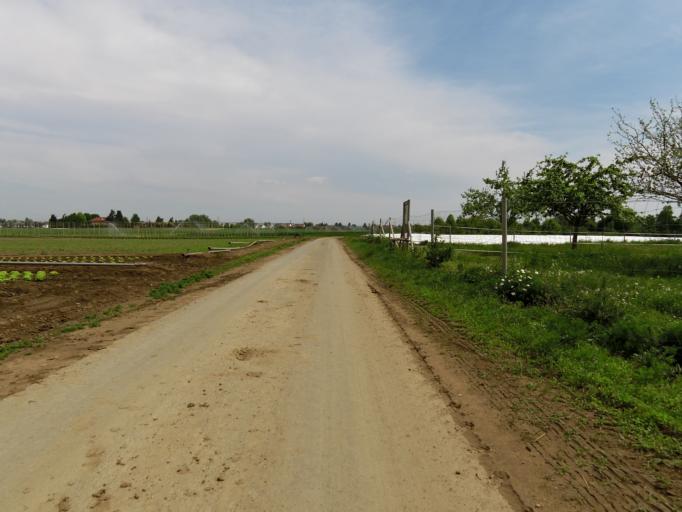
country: DE
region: Rheinland-Pfalz
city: Lambsheim
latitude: 49.5017
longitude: 8.2778
